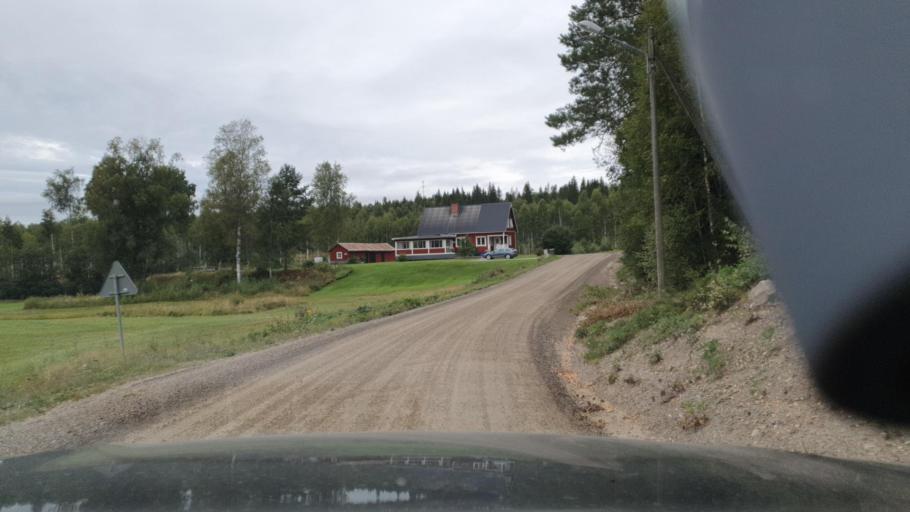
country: SE
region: Vaermland
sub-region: Arvika Kommun
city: Arvika
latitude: 59.9392
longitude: 12.6621
